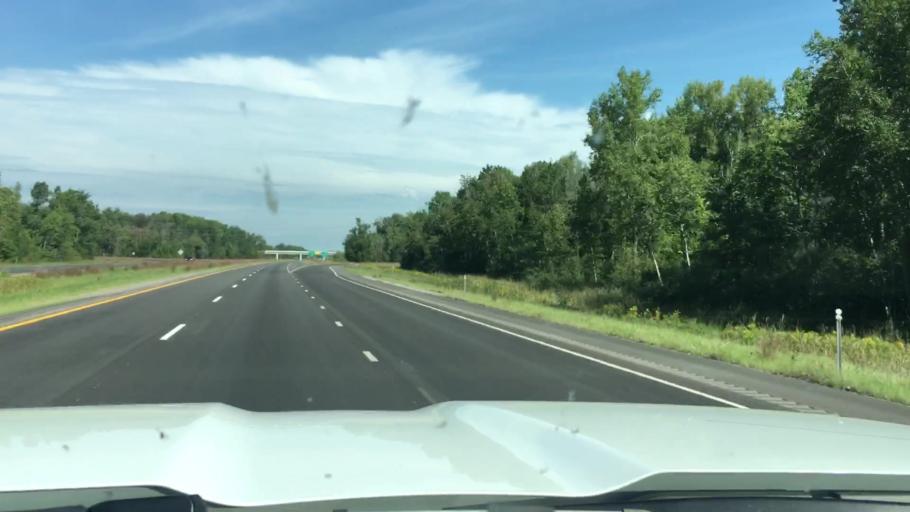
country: US
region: Michigan
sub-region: Saginaw County
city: Freeland
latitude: 43.5762
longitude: -84.1393
